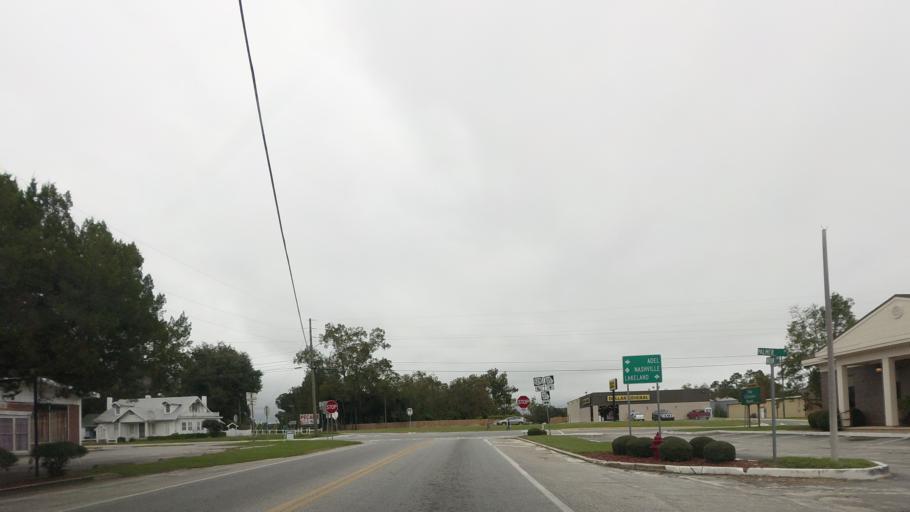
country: US
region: Georgia
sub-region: Berrien County
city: Ray City
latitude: 31.0743
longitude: -83.1995
